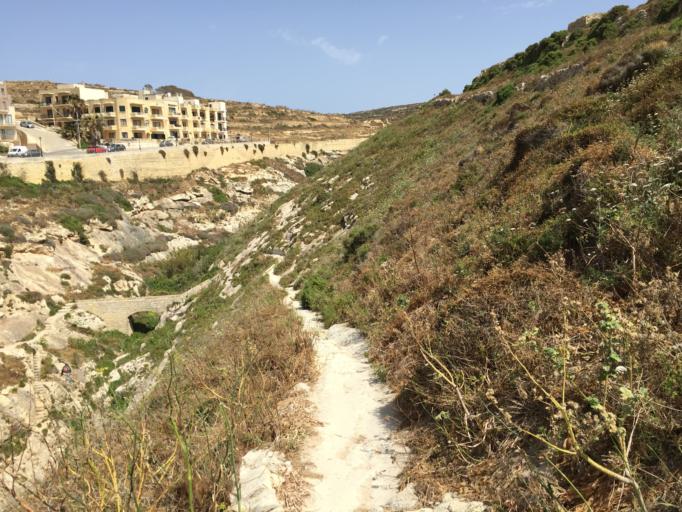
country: MT
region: Saint Lucia
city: Saint Lucia
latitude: 36.0272
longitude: 14.2157
